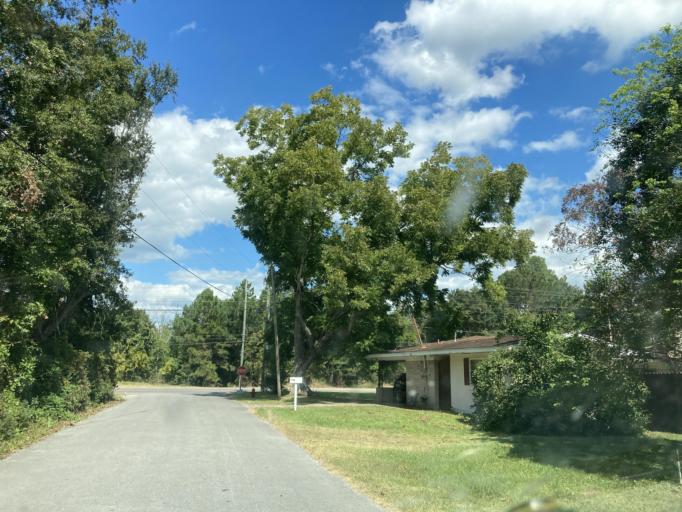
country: US
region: Mississippi
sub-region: Jackson County
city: Gulf Hills
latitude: 30.4426
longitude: -88.8509
